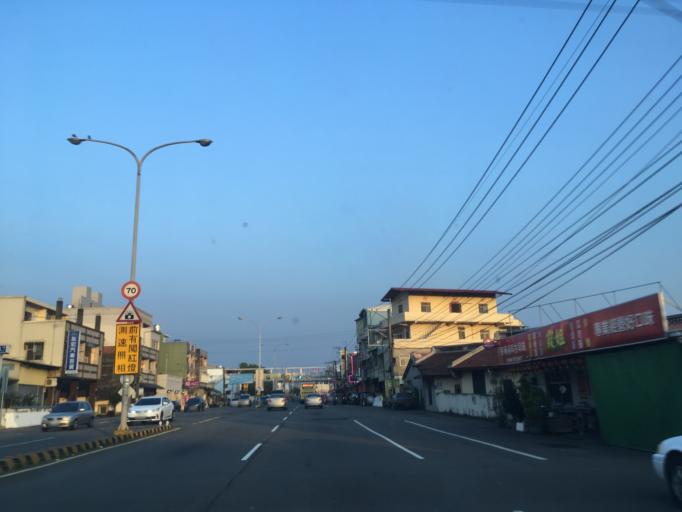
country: TW
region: Taiwan
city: Zhongxing New Village
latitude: 23.9972
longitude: 120.6627
